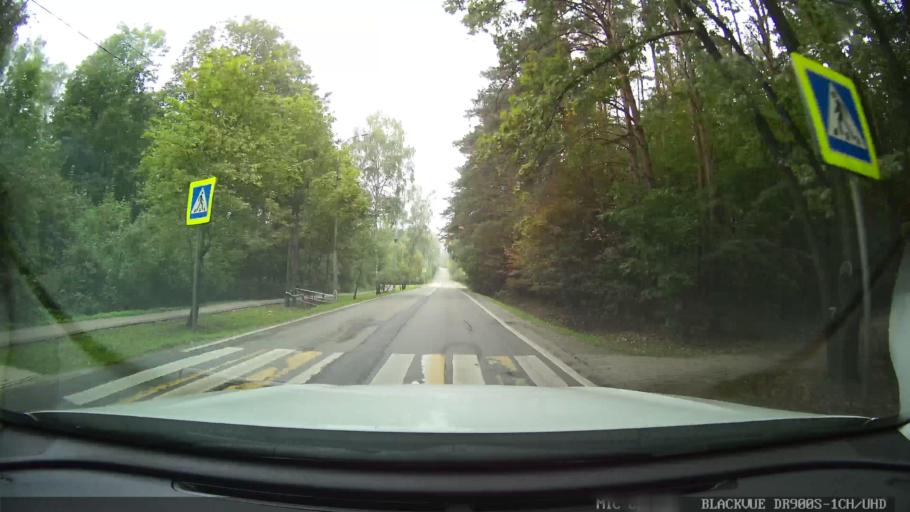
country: RU
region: Moscow
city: Solntsevo
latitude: 55.6474
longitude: 37.3618
